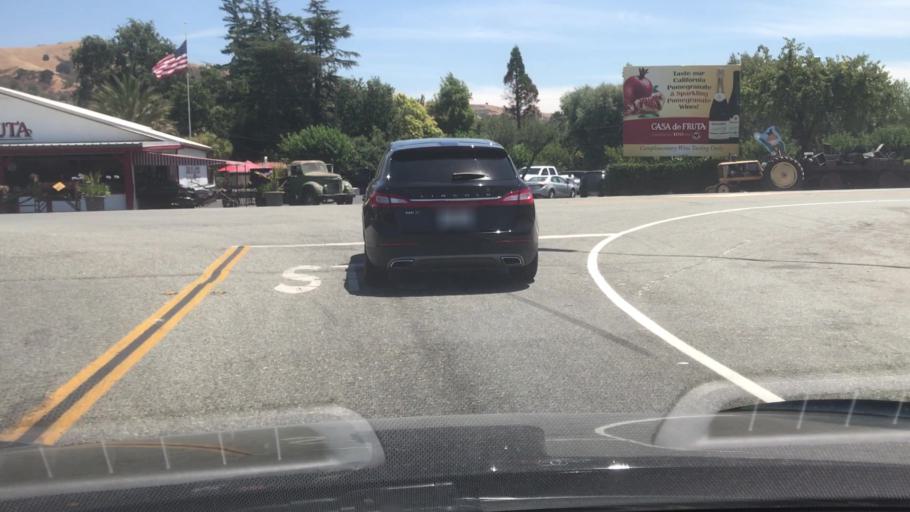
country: US
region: California
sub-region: San Benito County
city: Hollister
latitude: 36.9879
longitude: -121.3834
